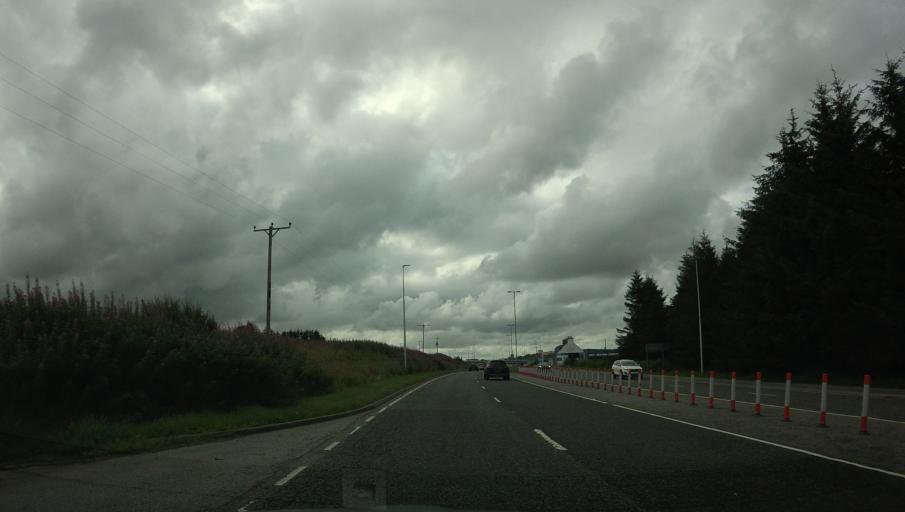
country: GB
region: Scotland
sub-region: Aberdeenshire
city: Westhill
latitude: 57.1464
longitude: -2.2351
